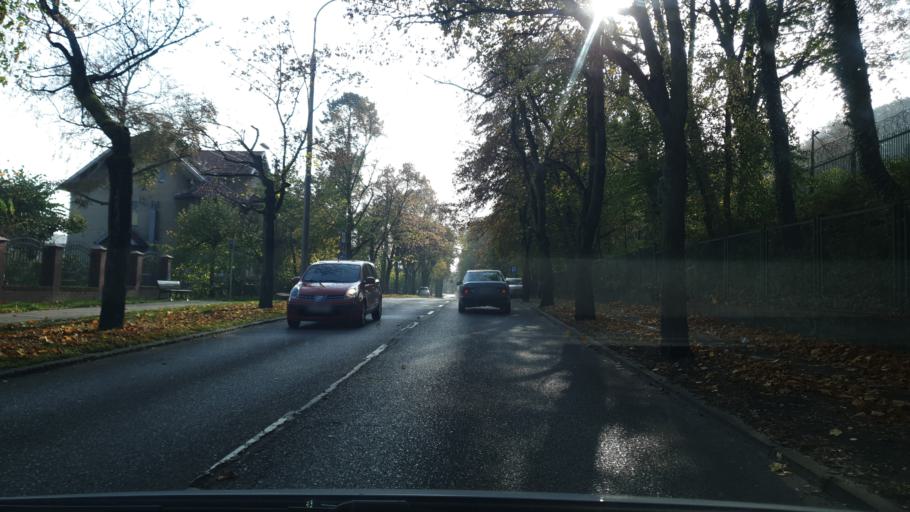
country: PL
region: Pomeranian Voivodeship
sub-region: Sopot
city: Sopot
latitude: 54.4006
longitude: 18.5623
